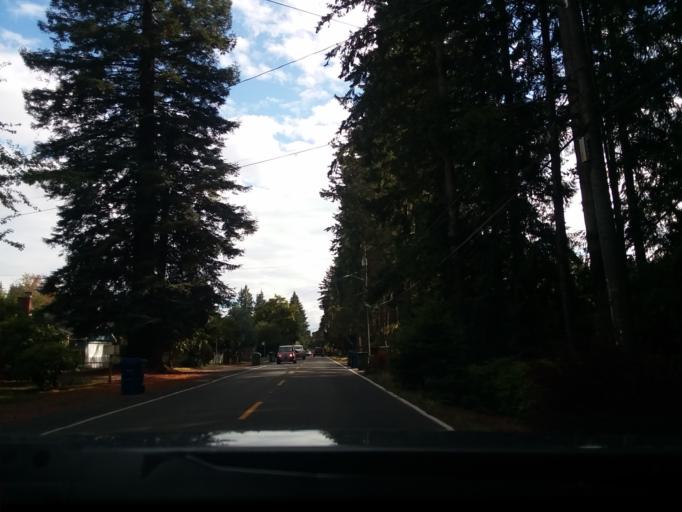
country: US
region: Washington
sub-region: King County
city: Shoreline
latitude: 47.7315
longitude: -122.3609
